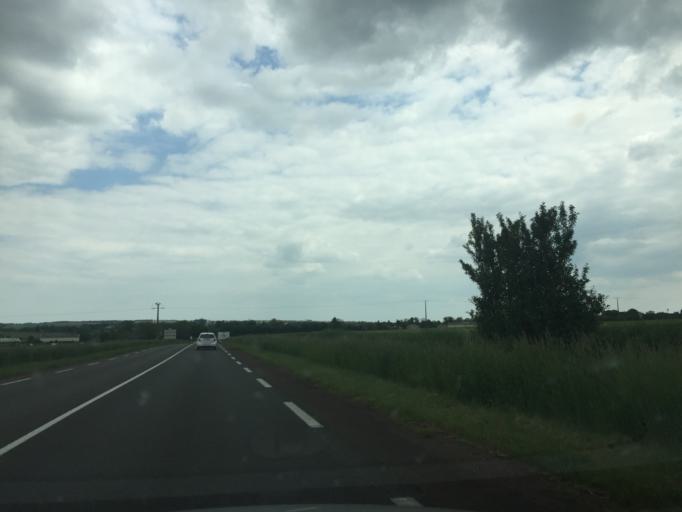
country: FR
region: Pays de la Loire
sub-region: Departement de la Vendee
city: Benet
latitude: 46.3791
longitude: -0.6018
